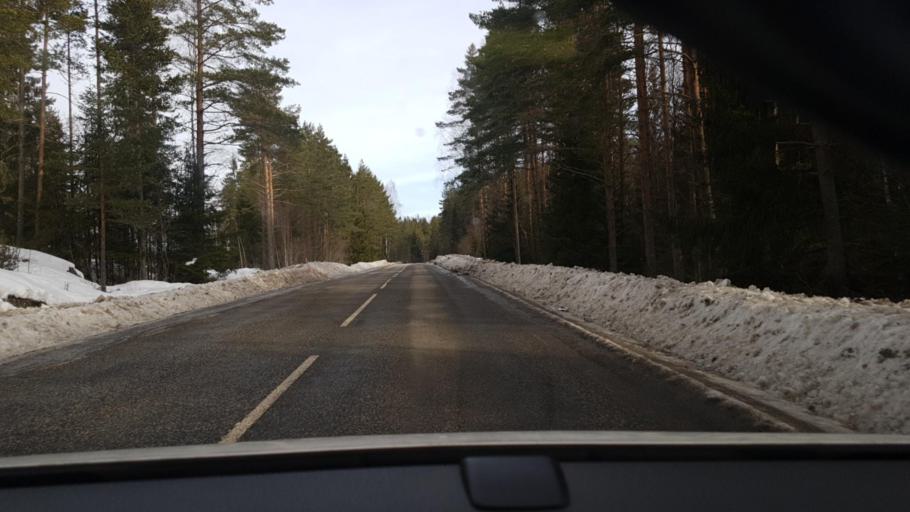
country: SE
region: Vaermland
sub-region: Eda Kommun
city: Amotfors
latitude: 59.5851
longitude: 12.2918
